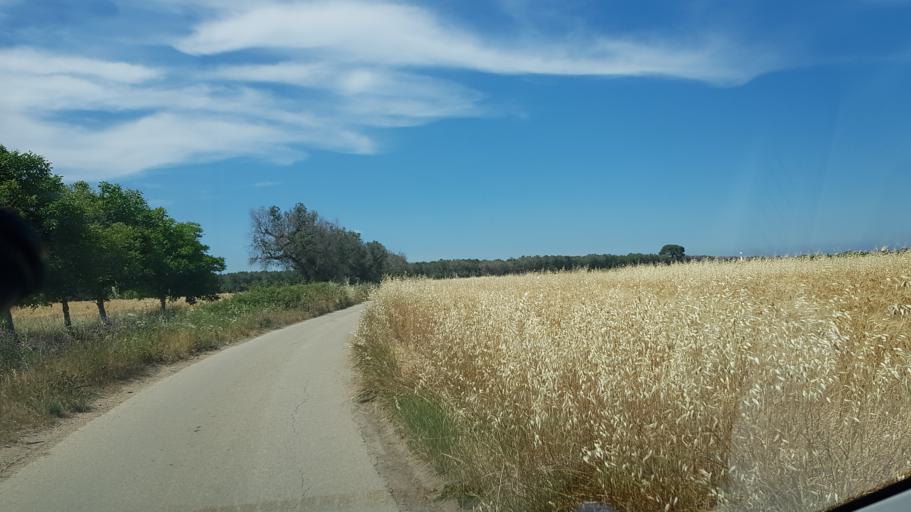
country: IT
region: Apulia
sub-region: Provincia di Brindisi
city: San Pietro Vernotico
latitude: 40.5340
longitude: 17.9969
